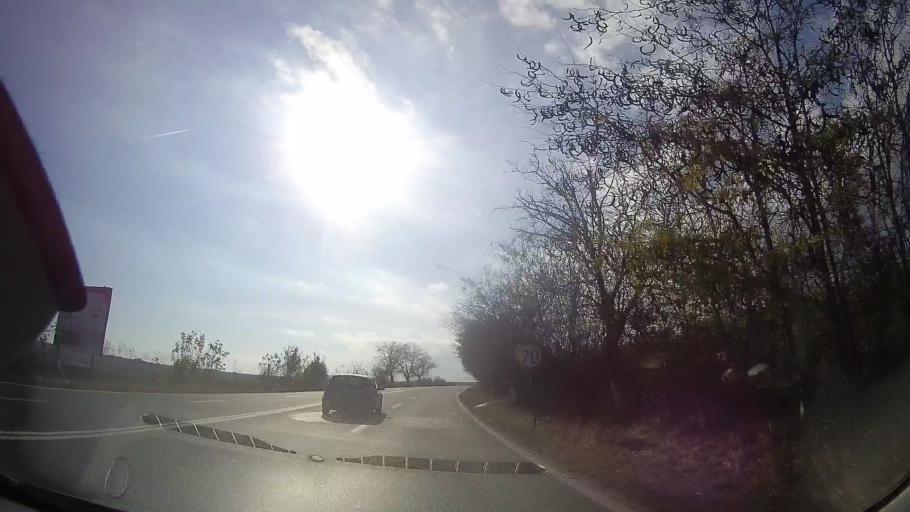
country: RO
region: Constanta
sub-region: Comuna Douazeci si Trei August
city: Douazeci si Trei August
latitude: 43.9109
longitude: 28.5772
